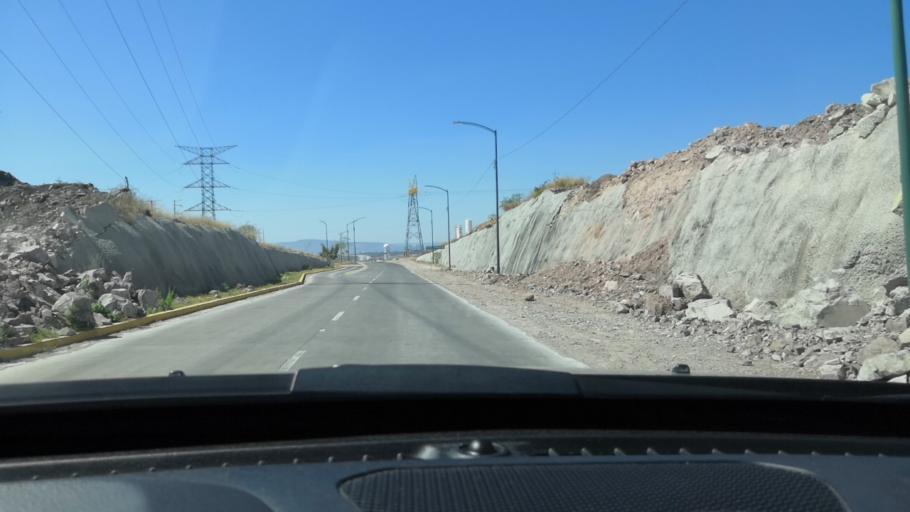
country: MX
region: Guanajuato
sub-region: Leon
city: Centro Familiar la Soledad
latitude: 21.1151
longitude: -101.7509
